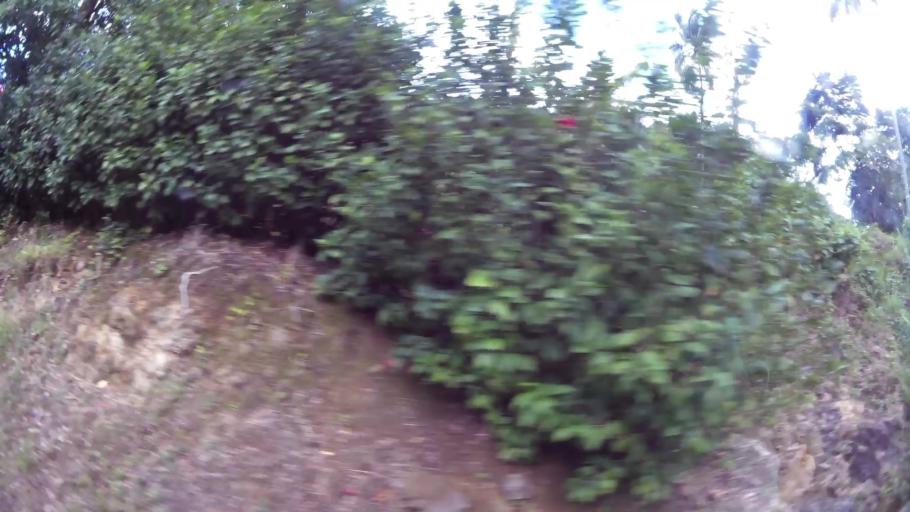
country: DM
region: Saint John
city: Portsmouth
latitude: 15.6210
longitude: -61.4603
